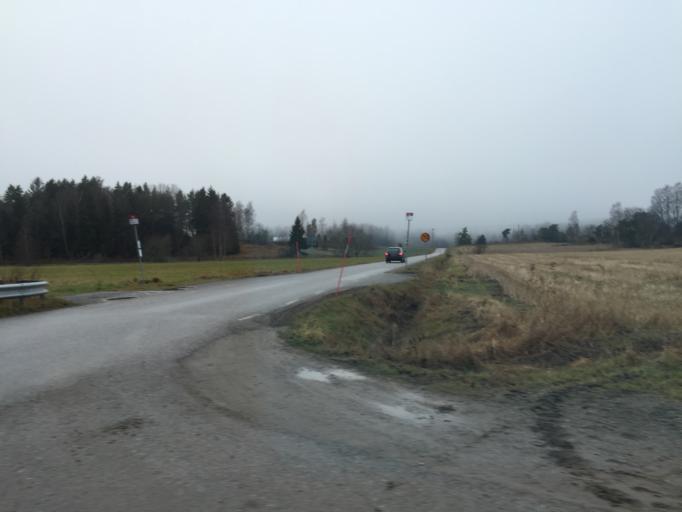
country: SE
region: Stockholm
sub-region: Nynashamns Kommun
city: Osmo
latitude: 59.0410
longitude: 17.8937
